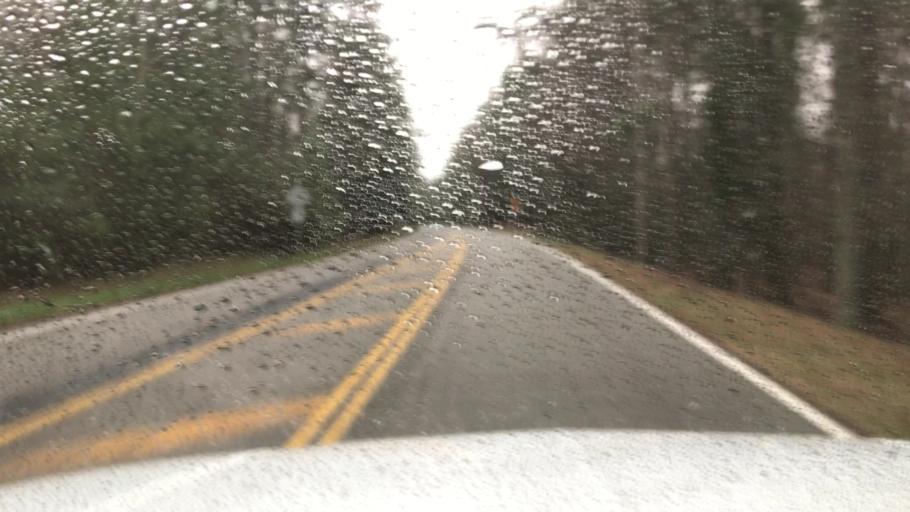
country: US
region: Virginia
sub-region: Henrico County
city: Short Pump
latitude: 37.6370
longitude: -77.6790
